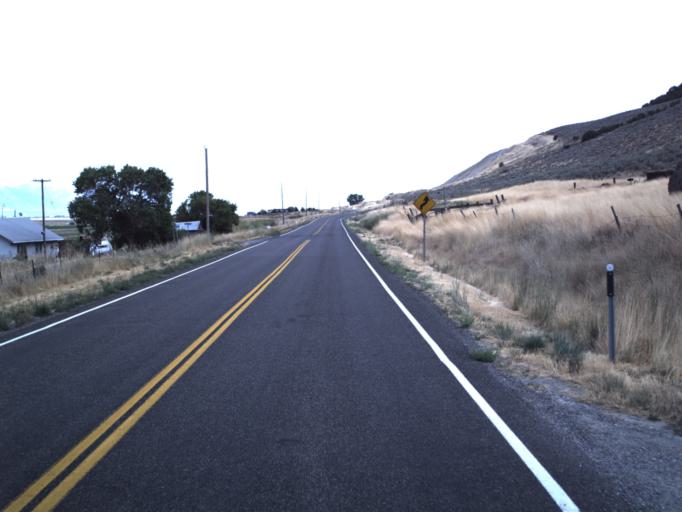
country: US
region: Utah
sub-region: Cache County
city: Benson
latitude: 41.9037
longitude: -111.9516
